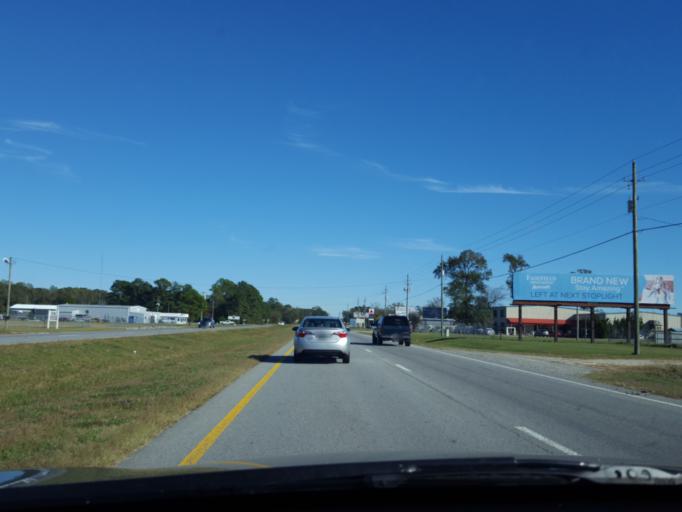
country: US
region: North Carolina
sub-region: Beaufort County
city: Washington
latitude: 35.6022
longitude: -77.1259
